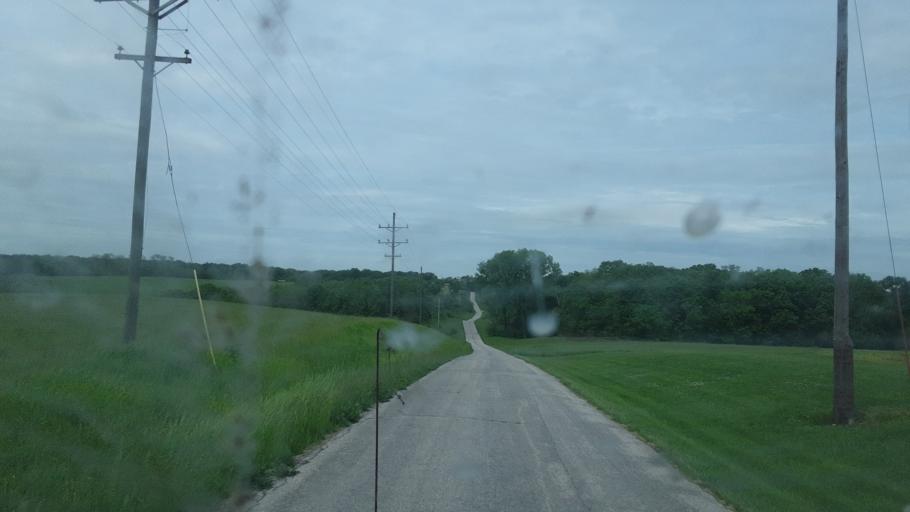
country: US
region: Missouri
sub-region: Clark County
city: Kahoka
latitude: 40.4240
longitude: -91.5969
